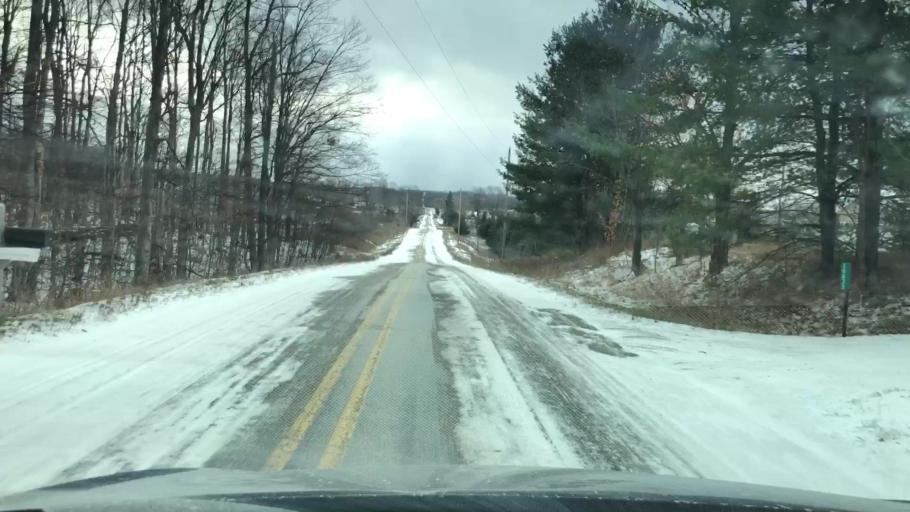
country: US
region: Michigan
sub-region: Antrim County
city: Elk Rapids
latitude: 44.9304
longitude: -85.5156
